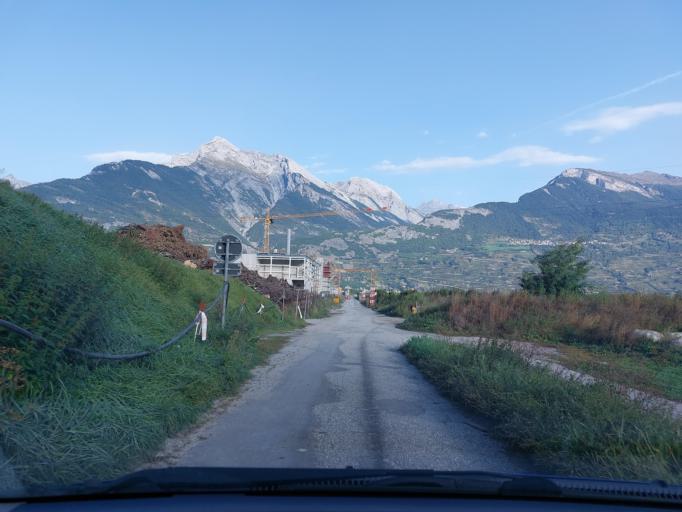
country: CH
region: Valais
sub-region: Conthey District
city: Vetroz
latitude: 46.2013
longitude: 7.2891
